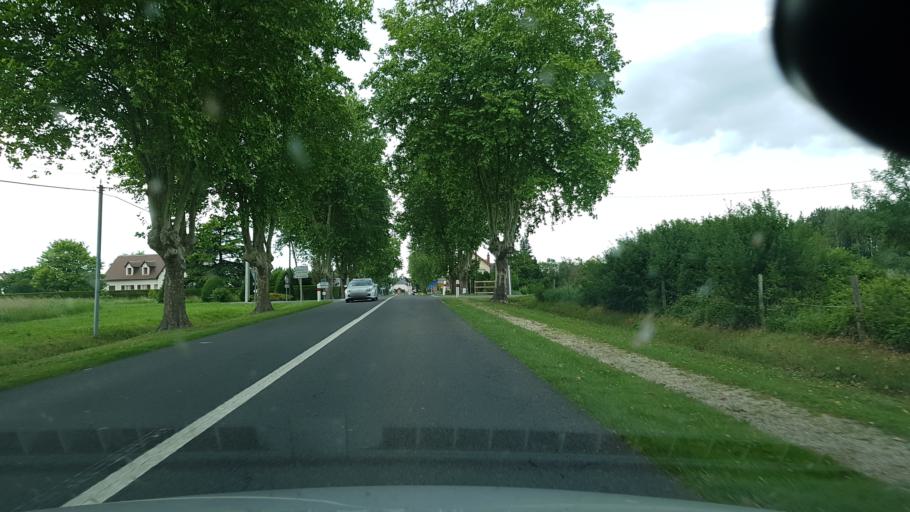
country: FR
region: Centre
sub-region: Departement du Loir-et-Cher
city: Chatillon-sur-Cher
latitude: 47.3394
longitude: 1.4822
